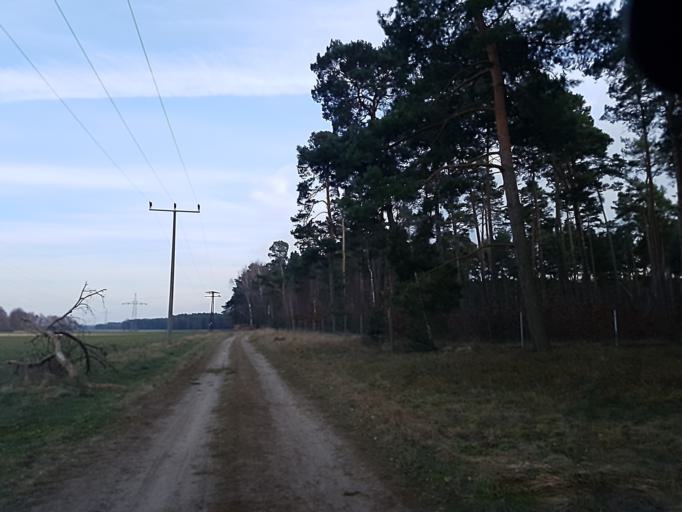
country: DE
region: Brandenburg
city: Wollin
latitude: 52.2606
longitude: 12.5252
